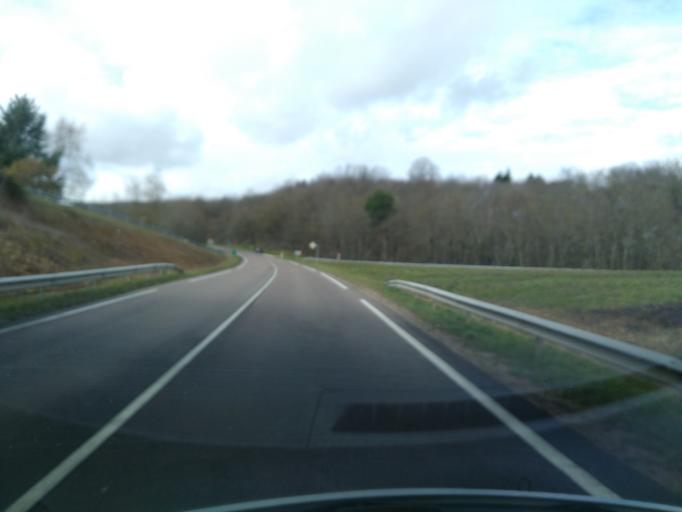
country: FR
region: Bourgogne
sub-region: Departement de Saone-et-Loire
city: Montcenis
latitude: 46.7899
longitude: 4.4028
